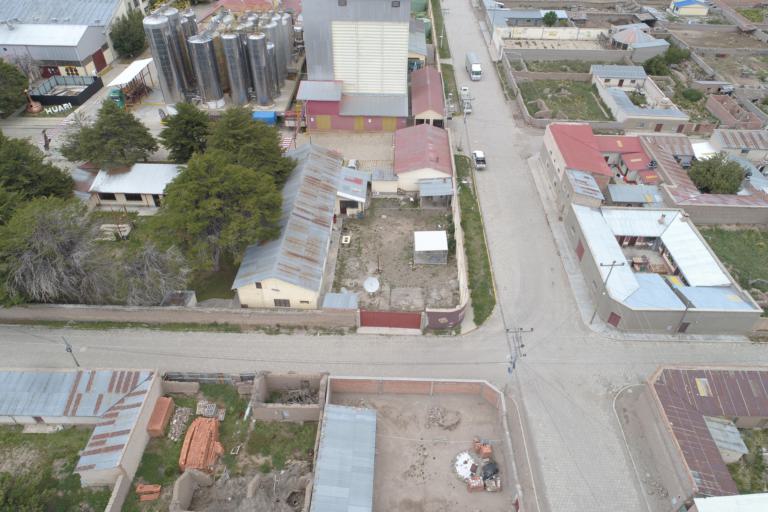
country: BO
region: Oruro
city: Challapata
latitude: -19.0125
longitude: -66.7799
